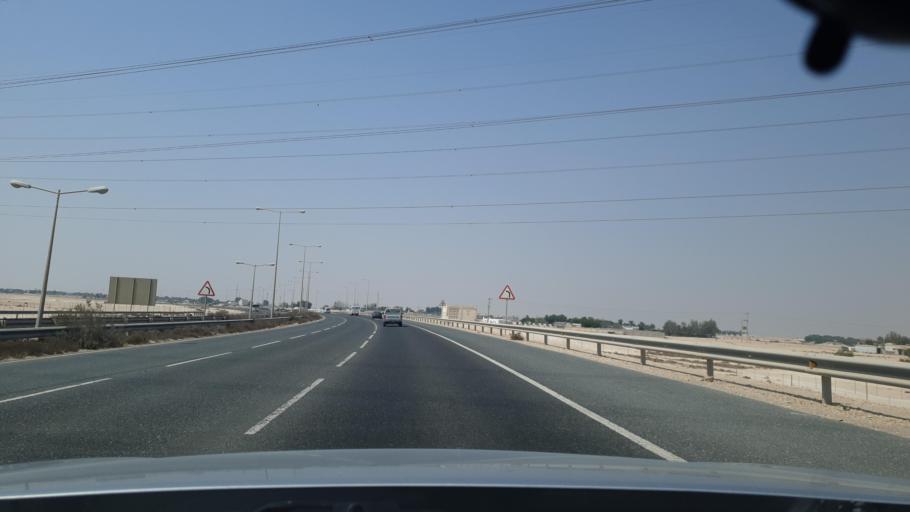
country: QA
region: Al Khawr
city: Al Khawr
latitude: 25.7561
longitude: 51.4726
